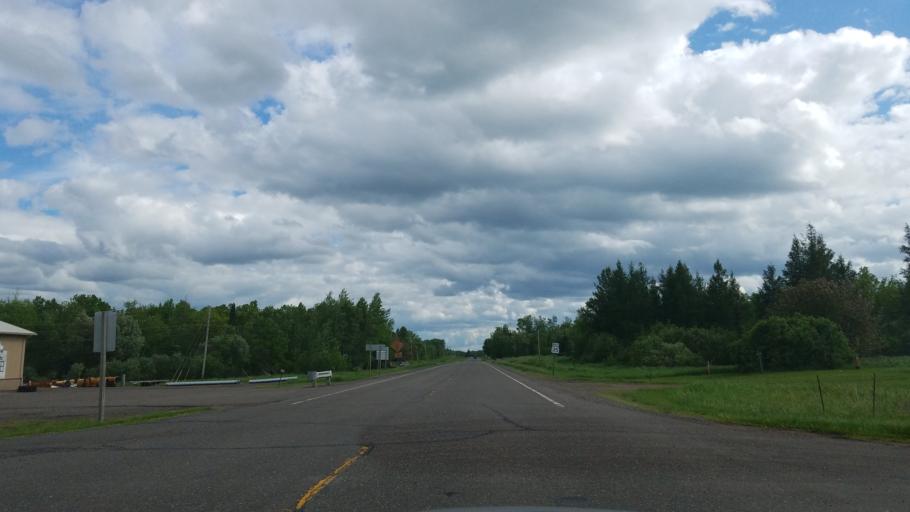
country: US
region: Wisconsin
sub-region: Washburn County
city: Spooner
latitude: 46.2162
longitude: -92.1546
